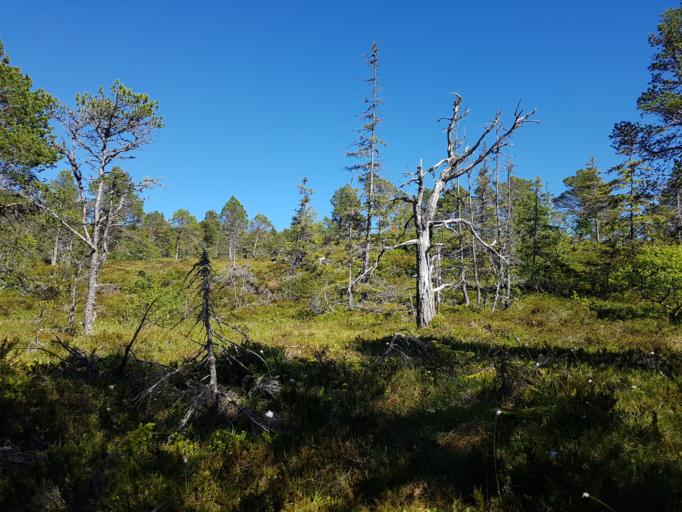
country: NO
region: Sor-Trondelag
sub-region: Melhus
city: Melhus
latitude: 63.4330
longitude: 10.2435
